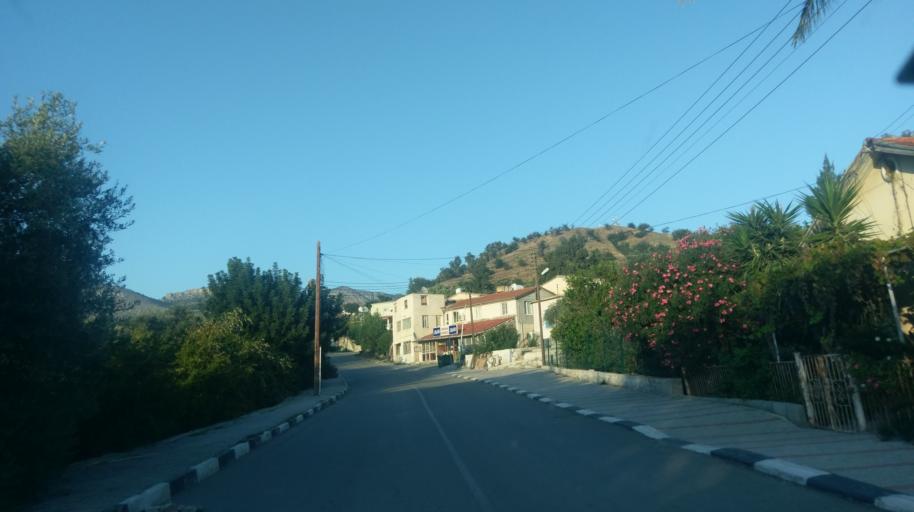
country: CY
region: Lefkosia
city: Nicosia
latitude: 35.2537
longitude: 33.4807
